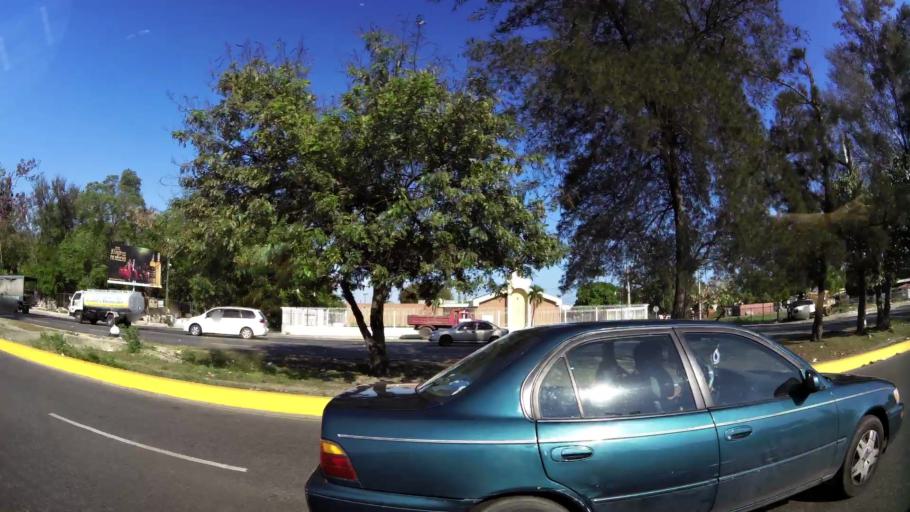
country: DO
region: Nacional
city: Bella Vista
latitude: 18.4751
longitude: -69.9680
